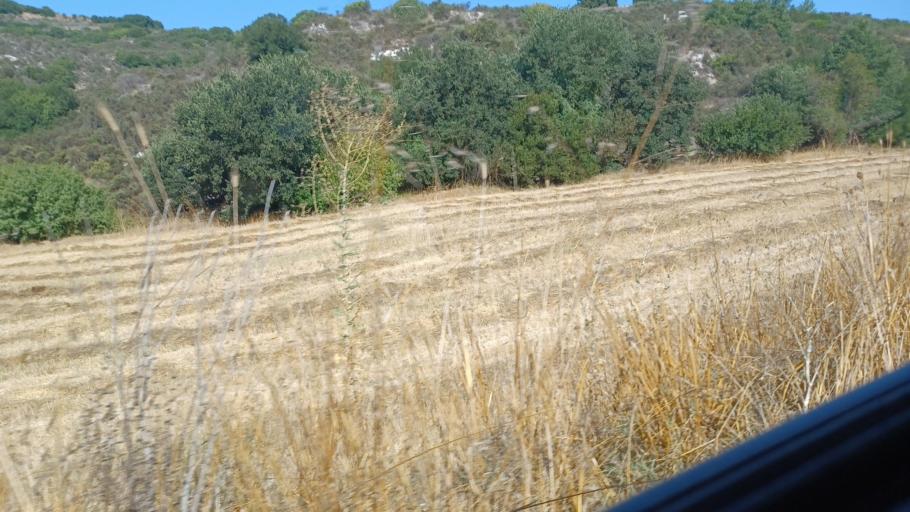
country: CY
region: Pafos
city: Mesogi
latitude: 34.8822
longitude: 32.5323
